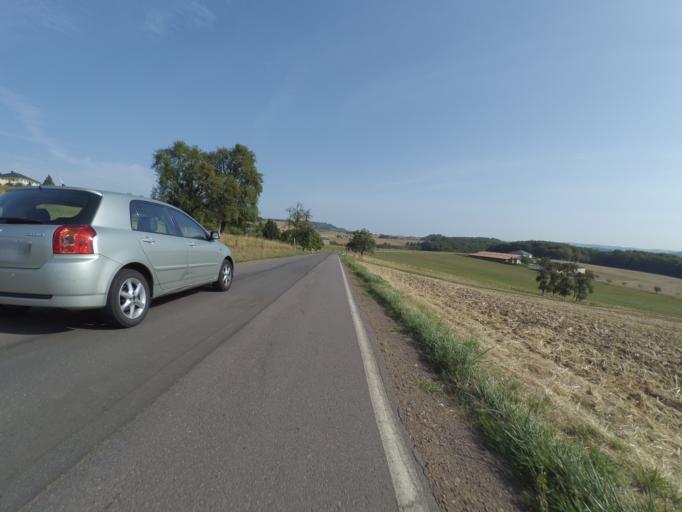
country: DE
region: Rheinland-Pfalz
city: Merzkirchen
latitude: 49.5738
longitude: 6.4936
